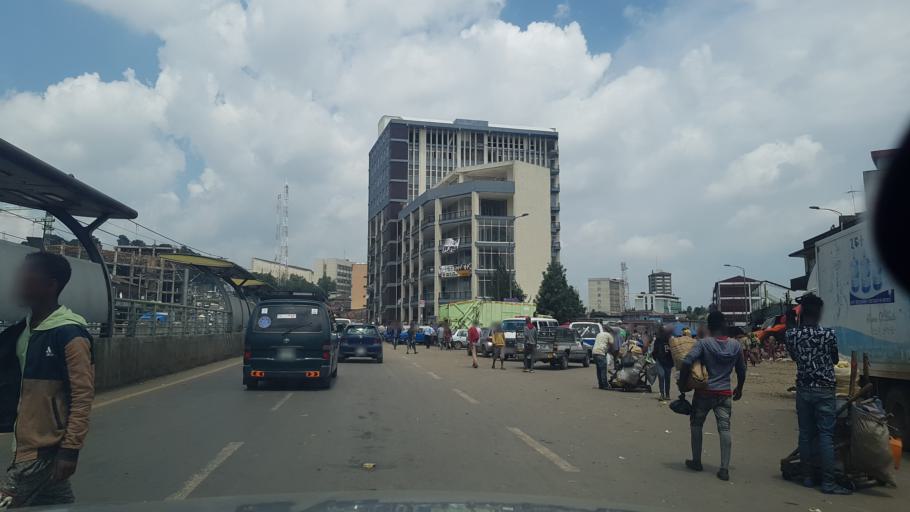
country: ET
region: Adis Abeba
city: Addis Ababa
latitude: 9.0345
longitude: 38.7467
